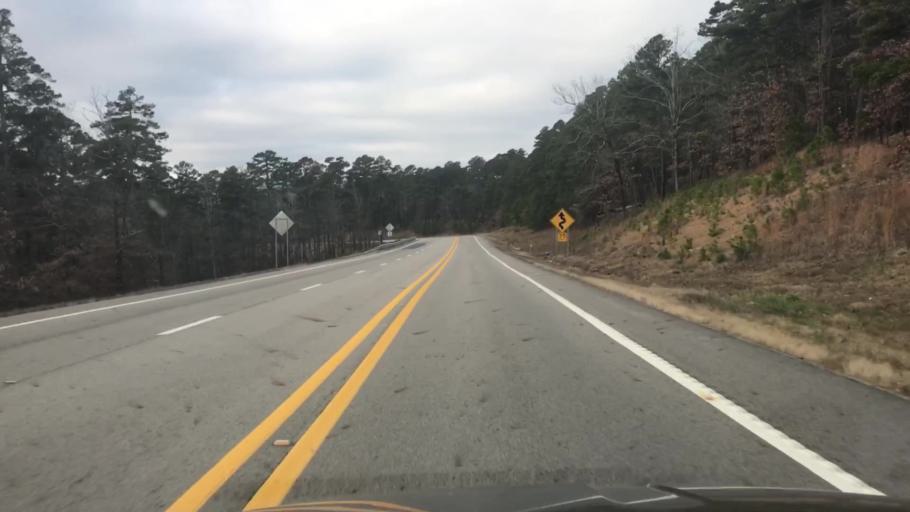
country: US
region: Arkansas
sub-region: Montgomery County
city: Mount Ida
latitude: 34.6834
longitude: -93.7914
